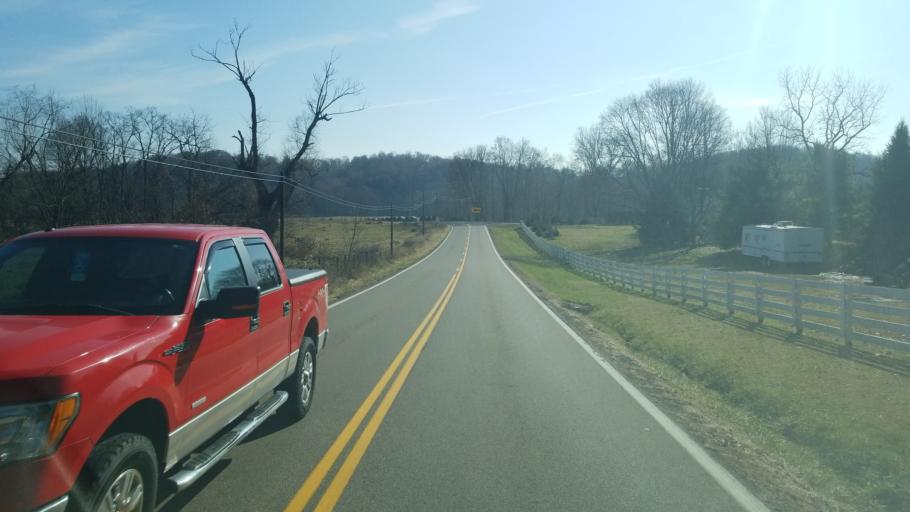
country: US
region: Ohio
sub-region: Licking County
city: Utica
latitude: 40.1652
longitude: -82.4860
